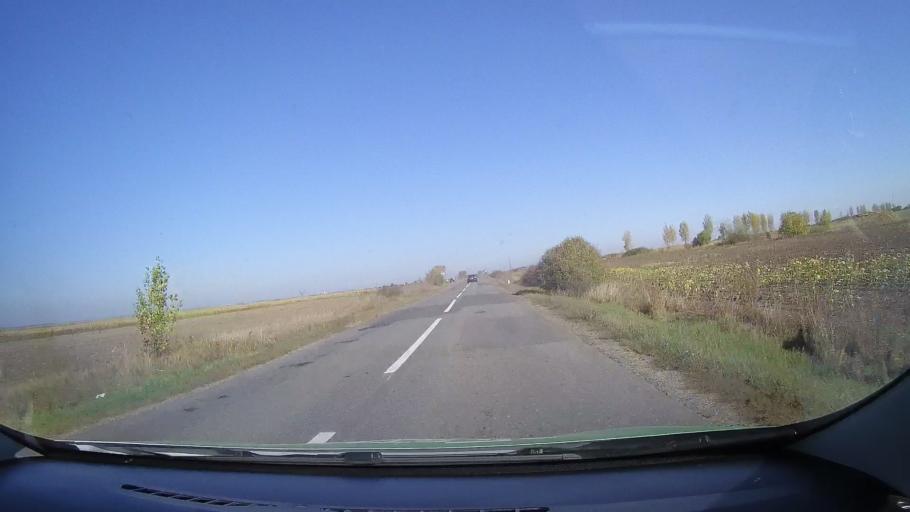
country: RO
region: Satu Mare
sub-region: Comuna Cauas
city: Cauas
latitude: 47.5950
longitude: 22.5466
